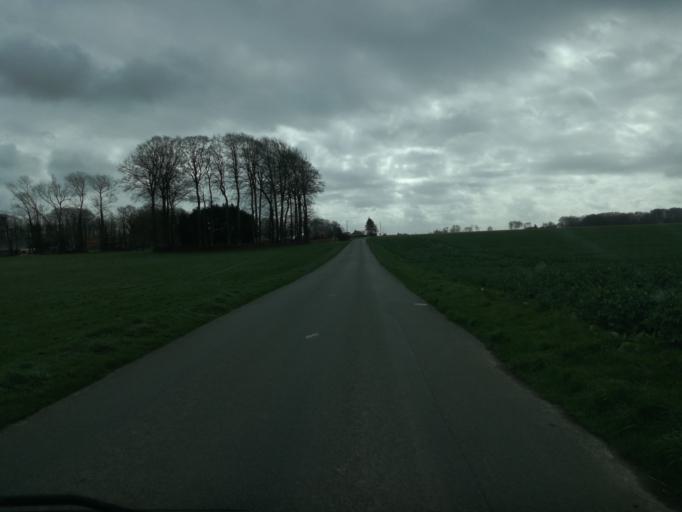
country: FR
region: Haute-Normandie
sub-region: Departement de la Seine-Maritime
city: Yebleron
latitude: 49.6715
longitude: 0.4952
